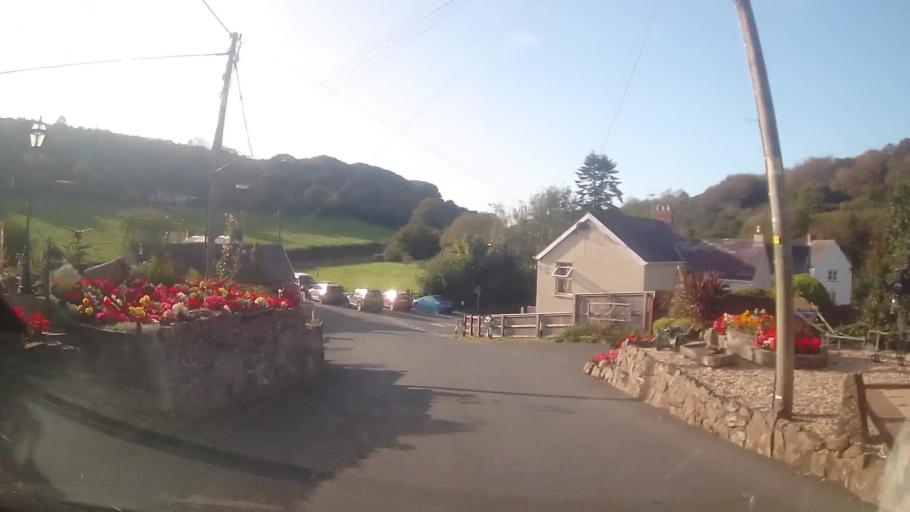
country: GB
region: Wales
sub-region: Pembrokeshire
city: Fishguard
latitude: 51.9802
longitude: -4.9322
